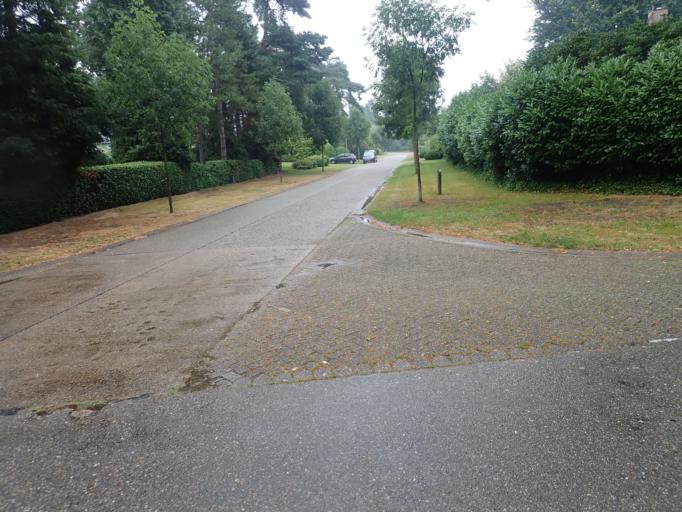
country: BE
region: Flanders
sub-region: Provincie Antwerpen
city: Schilde
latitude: 51.2278
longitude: 4.5604
